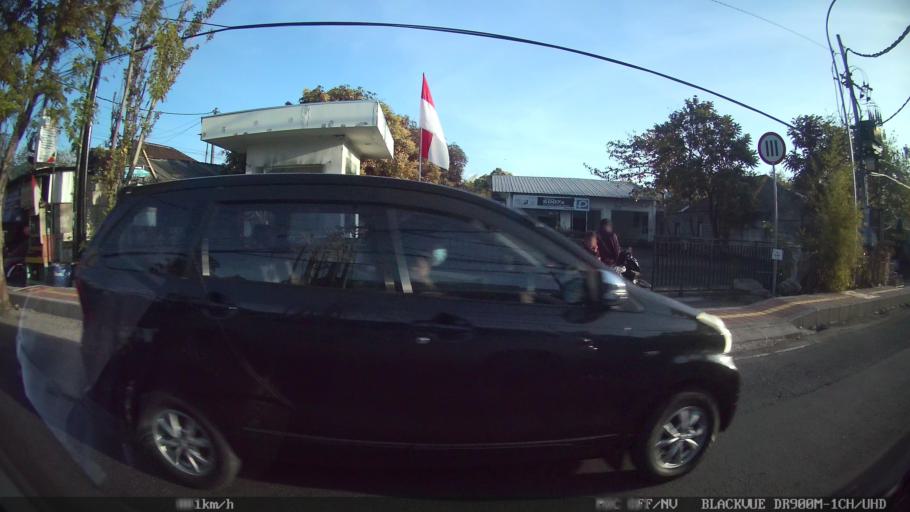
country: ID
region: Bali
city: Jimbaran
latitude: -8.7813
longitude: 115.1778
